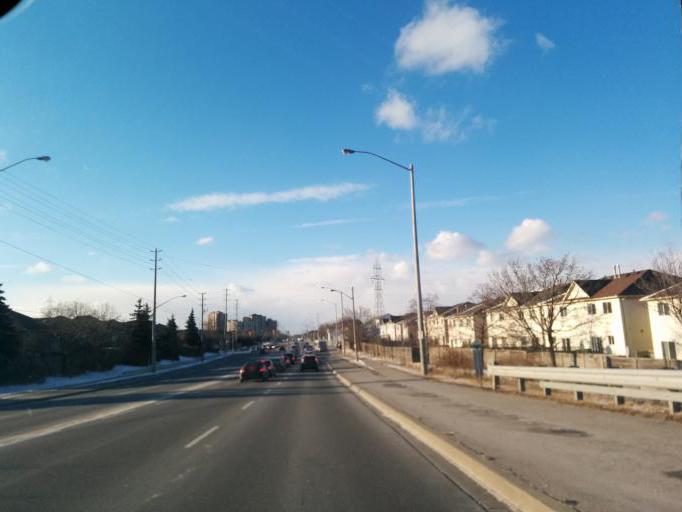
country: CA
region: Ontario
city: Brampton
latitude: 43.6466
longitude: -79.7302
